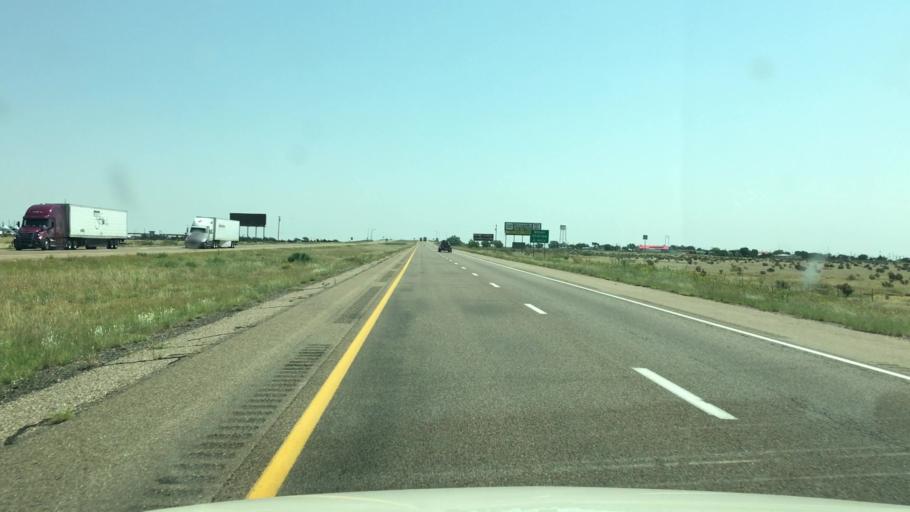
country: US
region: New Mexico
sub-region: Quay County
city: Logan
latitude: 35.1116
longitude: -103.3437
